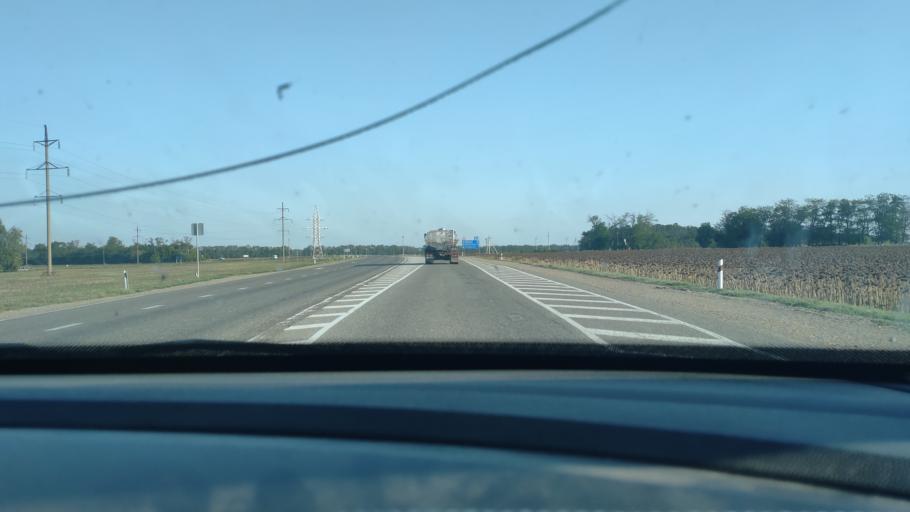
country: RU
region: Krasnodarskiy
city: Starominskaya
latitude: 46.5049
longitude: 39.0363
